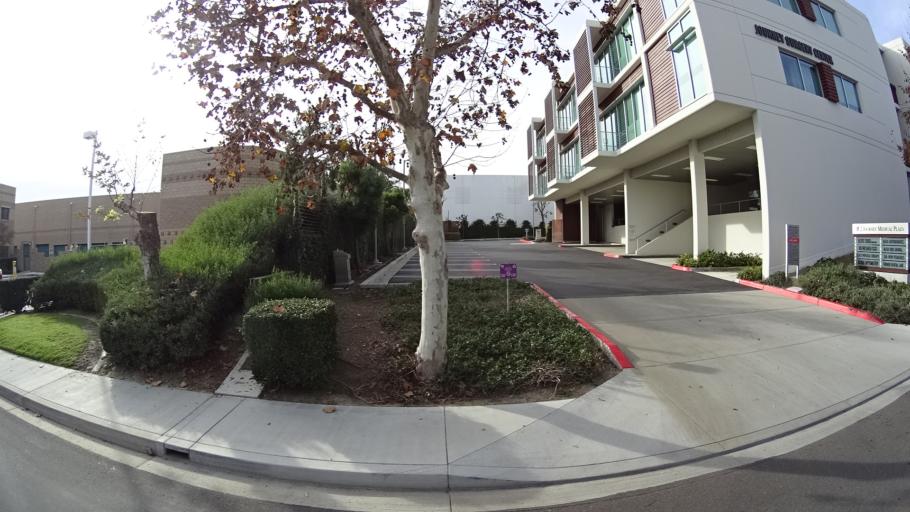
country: US
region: California
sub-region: Orange County
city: Aliso Viejo
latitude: 33.5690
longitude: -117.7264
